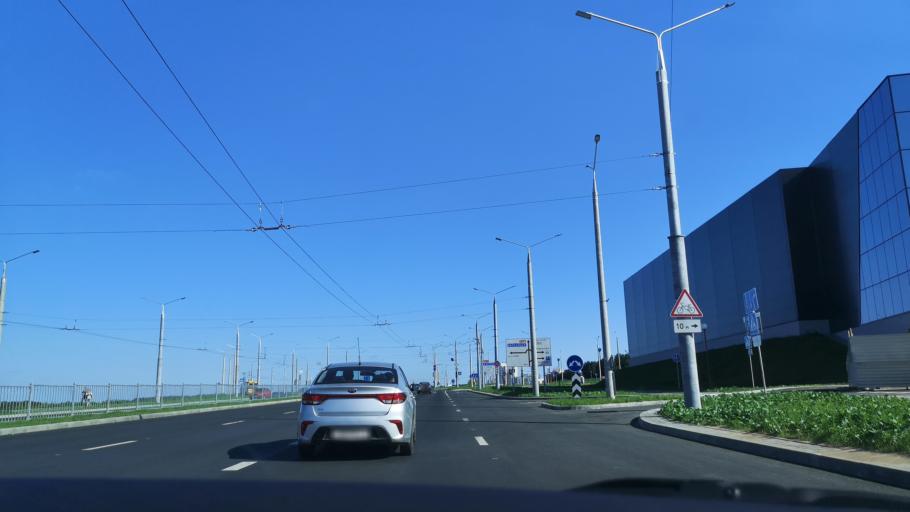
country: BY
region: Grodnenskaya
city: Hrodna
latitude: 53.6513
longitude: 23.8563
